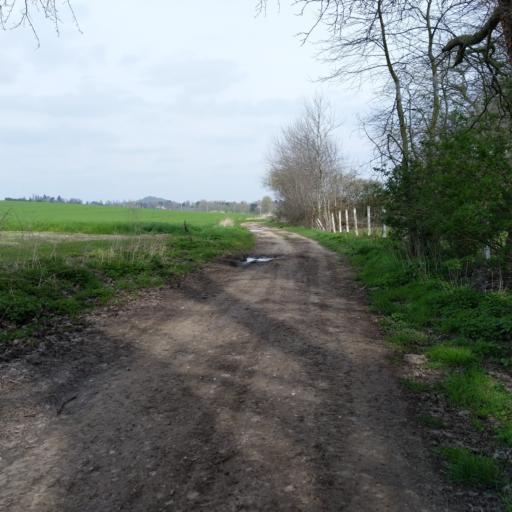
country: BE
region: Wallonia
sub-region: Province du Hainaut
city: Chasse Royale
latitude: 50.4058
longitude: 3.9324
